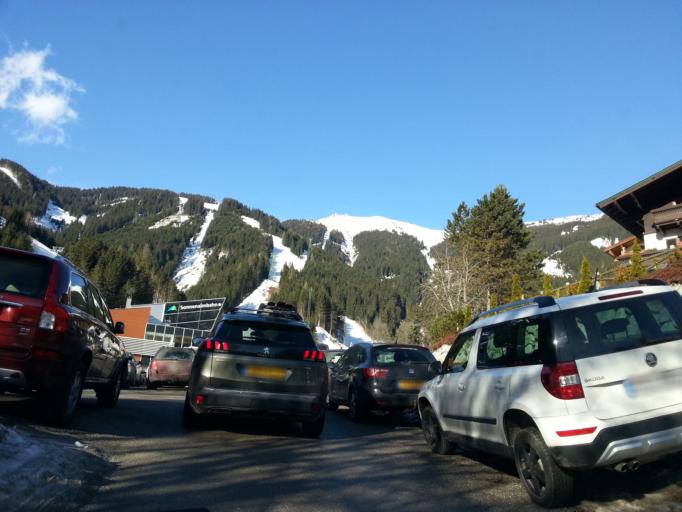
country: AT
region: Salzburg
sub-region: Politischer Bezirk Zell am See
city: Zell am See
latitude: 47.3271
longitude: 12.7730
